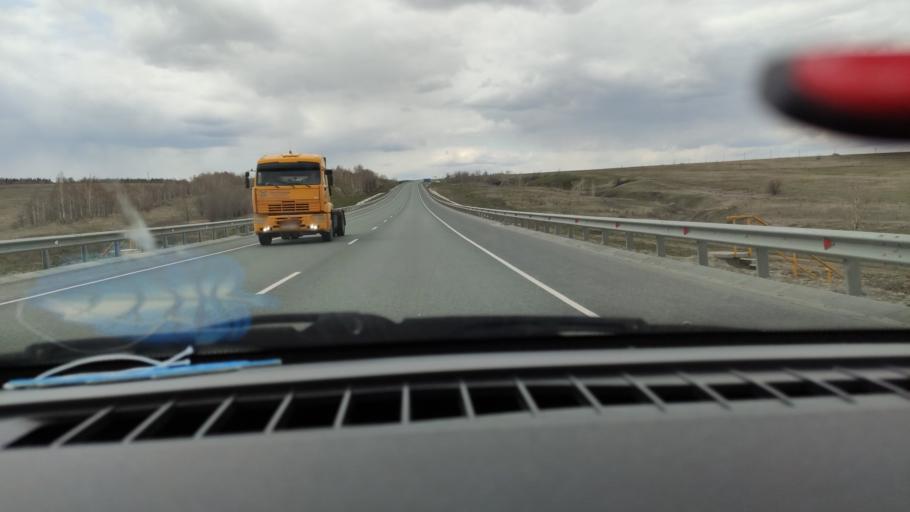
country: RU
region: Saratov
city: Shikhany
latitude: 52.1279
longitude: 47.2362
